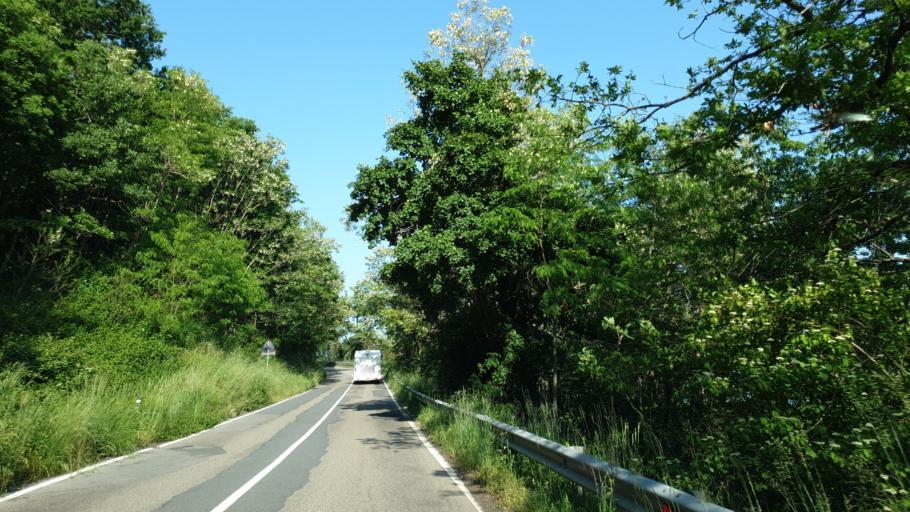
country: IT
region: Tuscany
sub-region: Province of Arezzo
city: Stia
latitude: 43.7744
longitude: 11.6955
